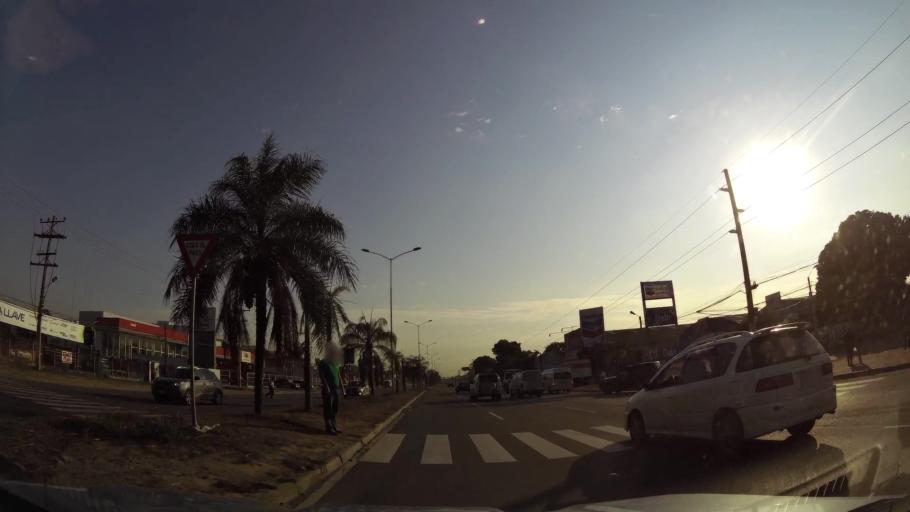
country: BO
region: Santa Cruz
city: Santa Cruz de la Sierra
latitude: -17.7205
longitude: -63.1637
